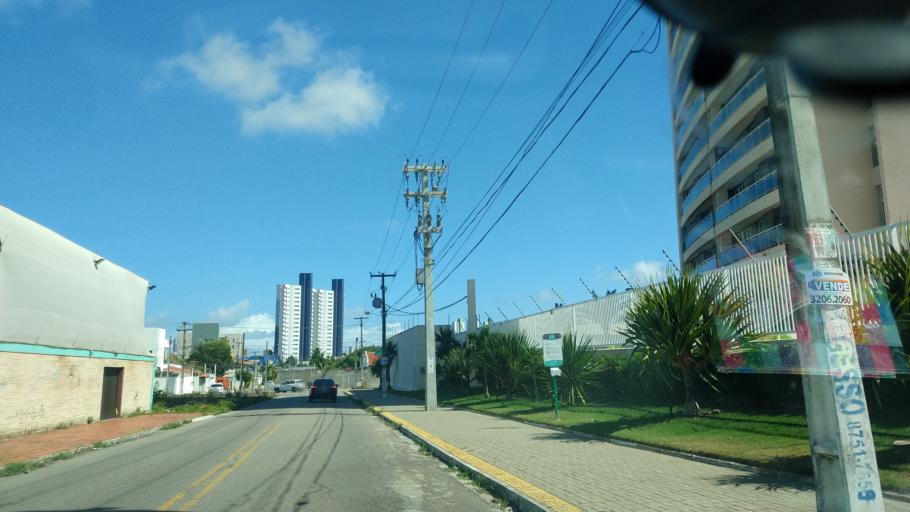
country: BR
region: Rio Grande do Norte
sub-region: Natal
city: Natal
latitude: -5.8694
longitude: -35.1941
